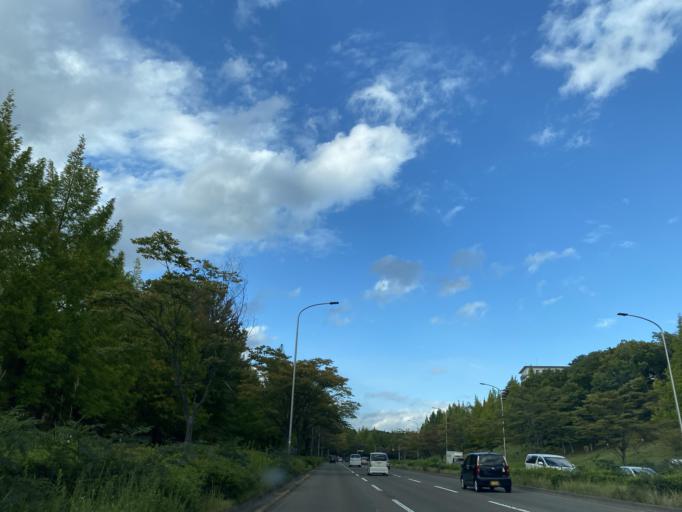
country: JP
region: Miyagi
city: Tomiya
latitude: 38.3378
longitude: 140.8392
